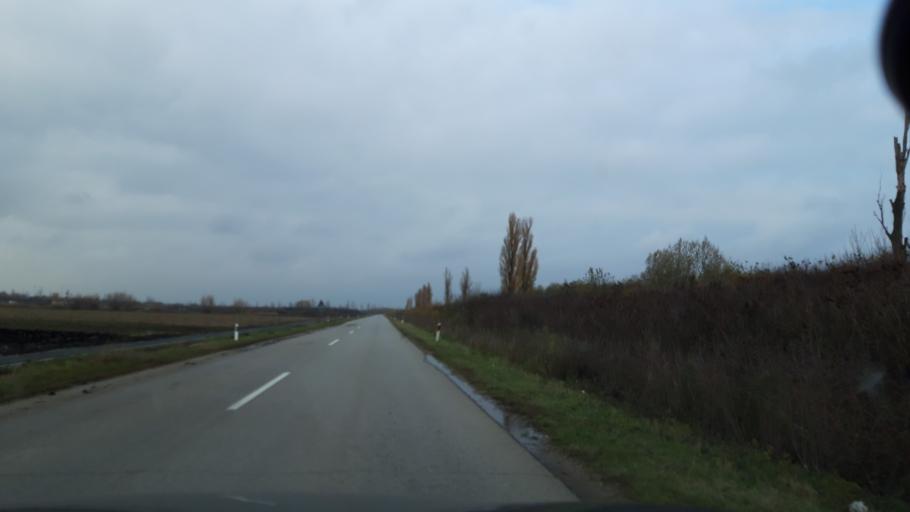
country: RS
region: Autonomna Pokrajina Vojvodina
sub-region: Severnobanatski Okrug
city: Novi Knezevac
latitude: 46.0689
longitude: 20.1033
